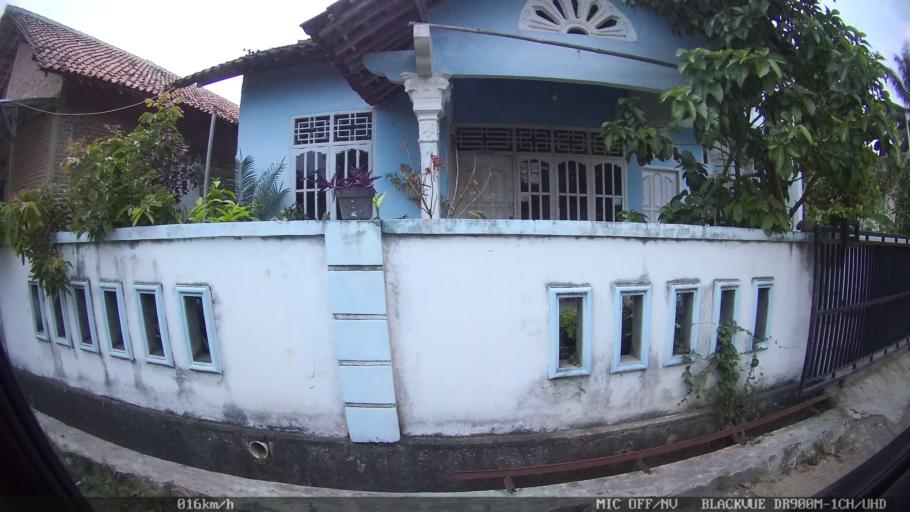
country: ID
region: Lampung
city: Pringsewu
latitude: -5.3450
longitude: 104.9815
